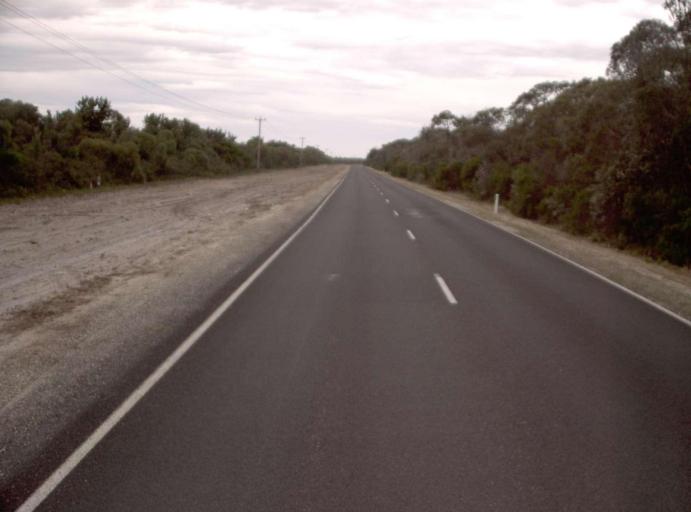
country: AU
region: Victoria
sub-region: East Gippsland
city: Bairnsdale
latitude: -38.0928
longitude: 147.5167
